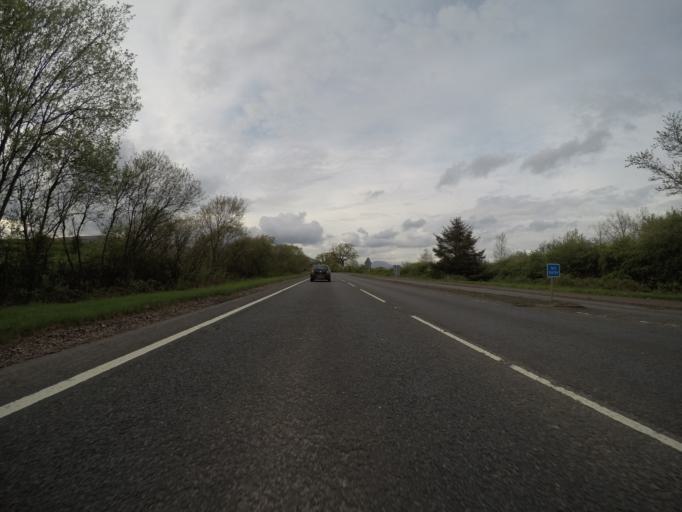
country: GB
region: Scotland
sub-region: West Dunbartonshire
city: Balloch
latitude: 56.0285
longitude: -4.6344
